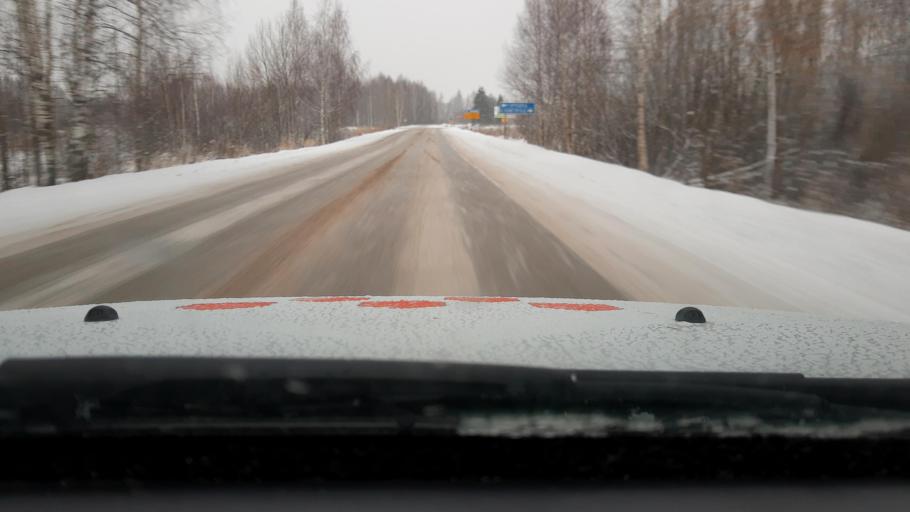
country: RU
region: Nizjnij Novgorod
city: Neklyudovo
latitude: 56.5264
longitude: 43.8327
